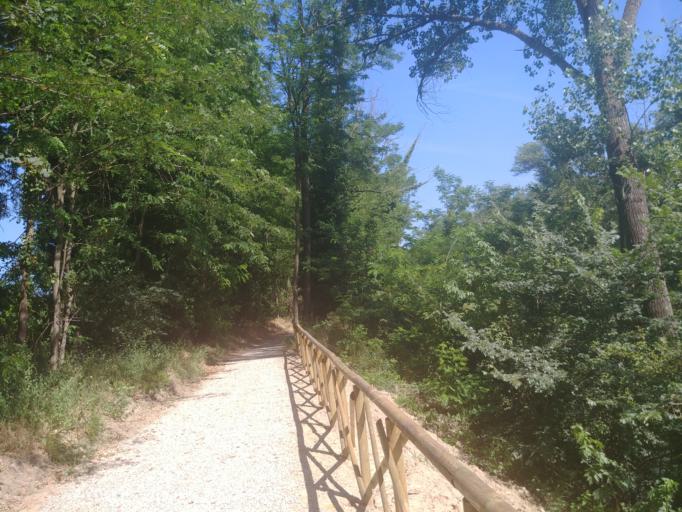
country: IT
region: Umbria
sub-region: Provincia di Perugia
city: Ponte Felcino
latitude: 43.1076
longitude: 12.4501
